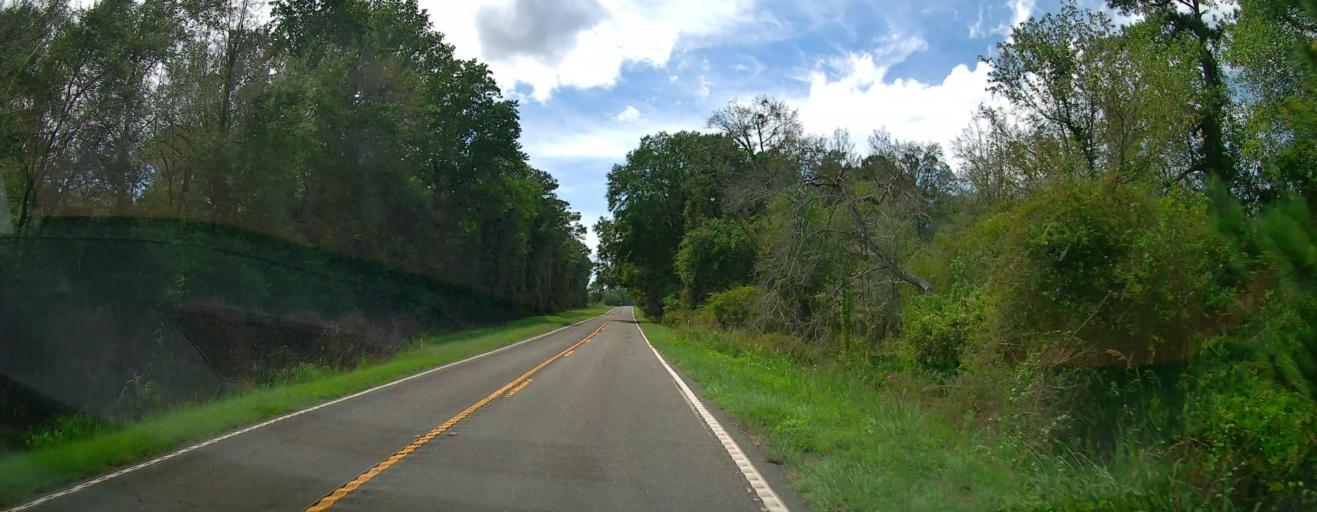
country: US
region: Georgia
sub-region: Taylor County
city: Reynolds
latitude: 32.4411
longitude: -84.1098
